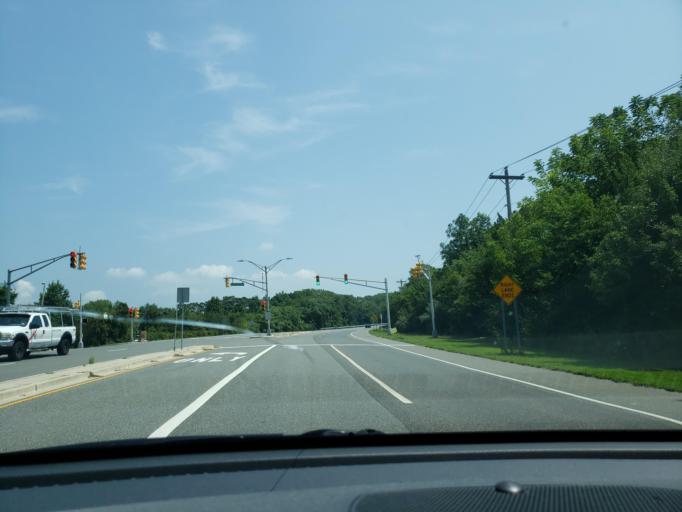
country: US
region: New Jersey
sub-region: Cape May County
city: North Cape May
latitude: 38.9739
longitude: -74.9364
